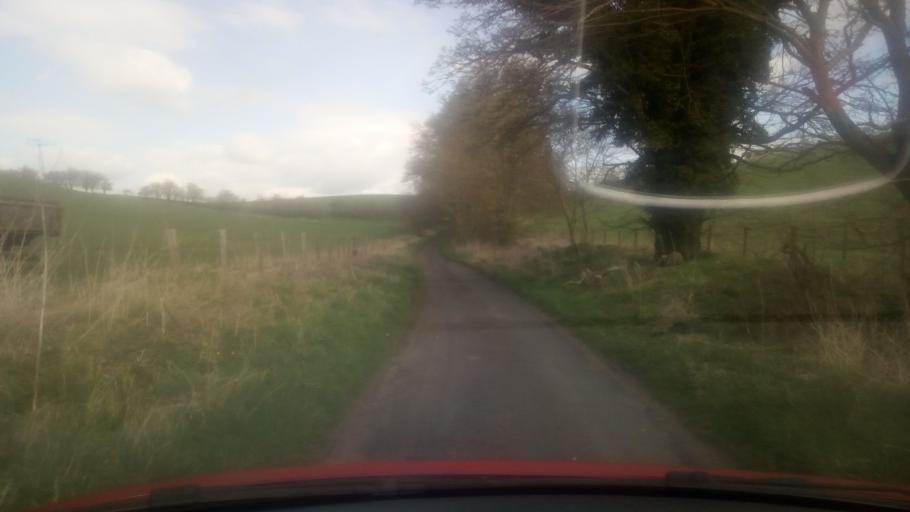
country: GB
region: Scotland
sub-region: The Scottish Borders
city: Jedburgh
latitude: 55.4924
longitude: -2.5391
